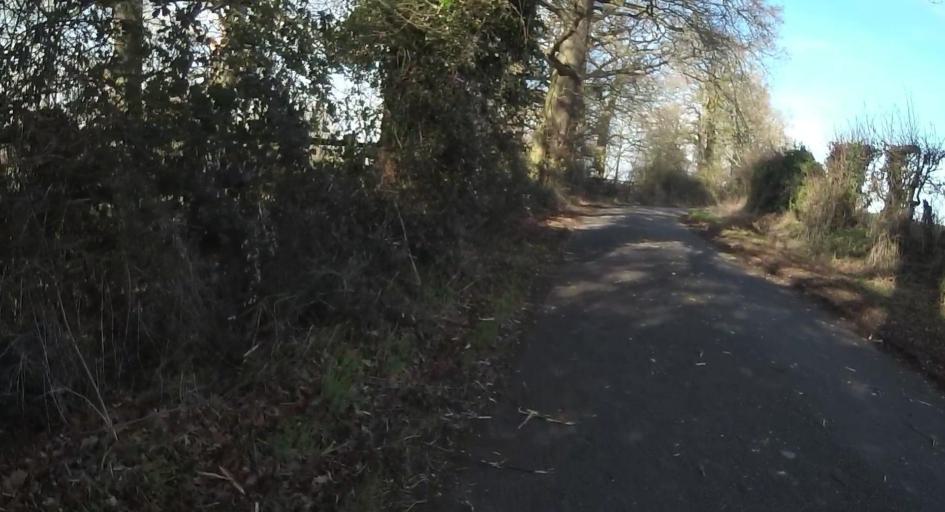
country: GB
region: England
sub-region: West Berkshire
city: Stratfield Mortimer
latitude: 51.3759
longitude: -1.0030
